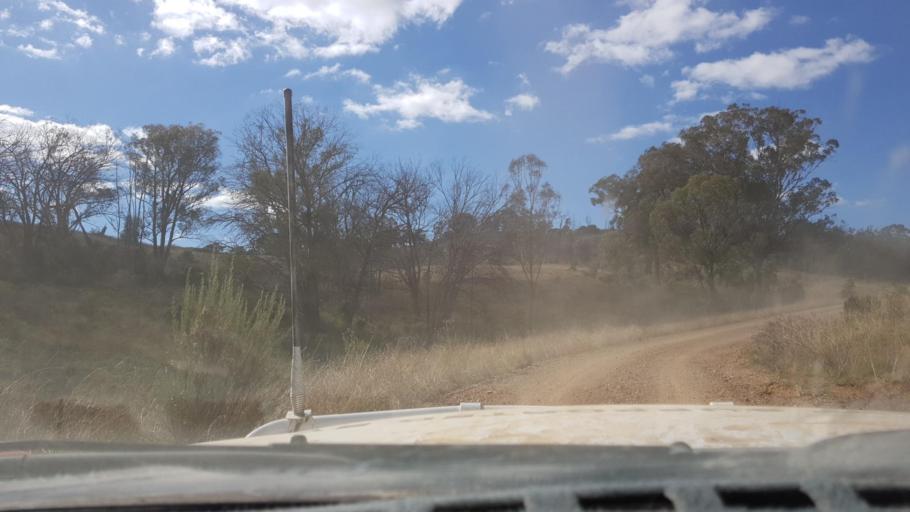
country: AU
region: New South Wales
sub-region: Tamworth Municipality
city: Manilla
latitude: -30.4377
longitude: 150.8404
